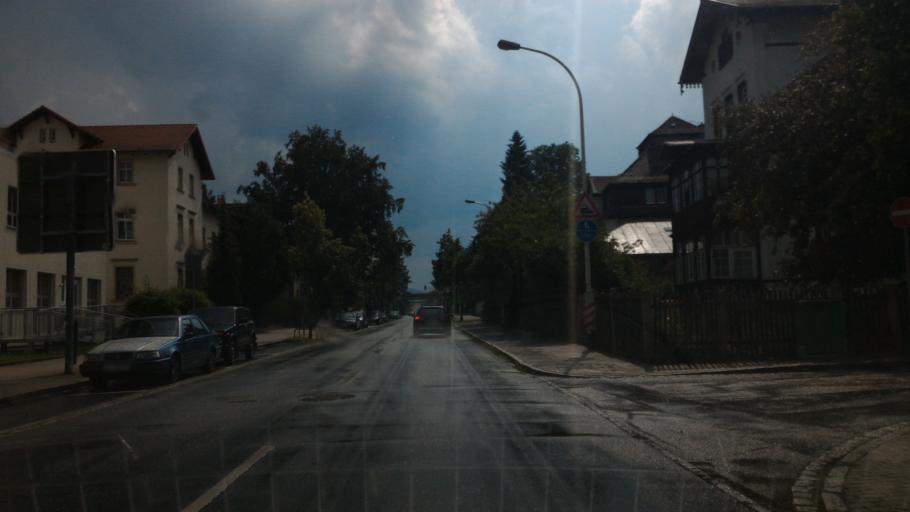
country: DE
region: Saxony
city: Zittau
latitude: 50.8998
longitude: 14.8203
